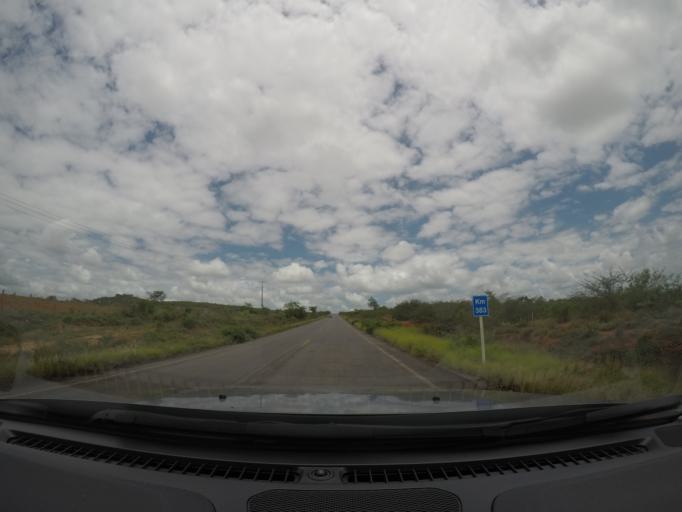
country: BR
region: Bahia
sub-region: Itaberaba
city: Itaberaba
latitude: -12.4571
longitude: -40.1564
